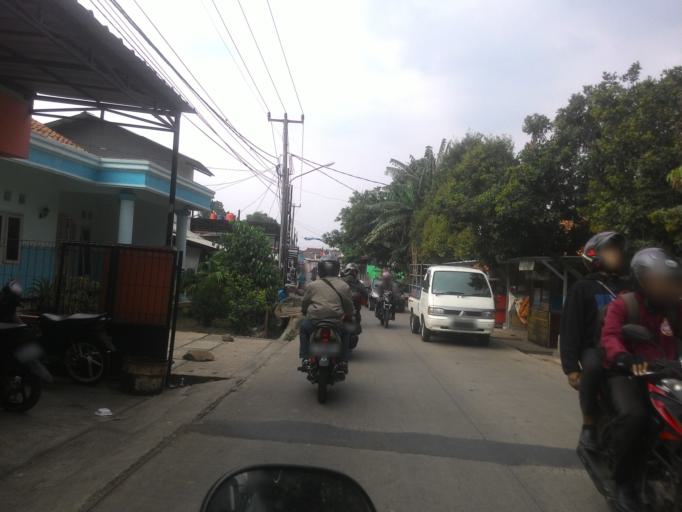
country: ID
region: West Java
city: Cibinong
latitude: -6.4551
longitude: 106.8395
